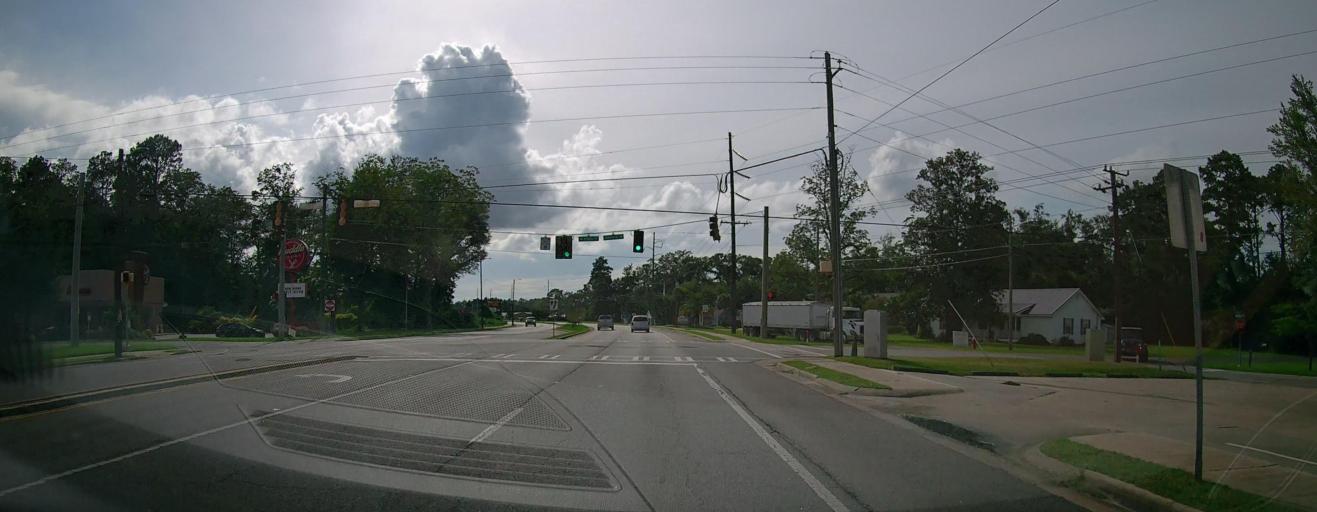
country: US
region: Georgia
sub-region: Wayne County
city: Jesup
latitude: 31.6035
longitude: -81.9001
